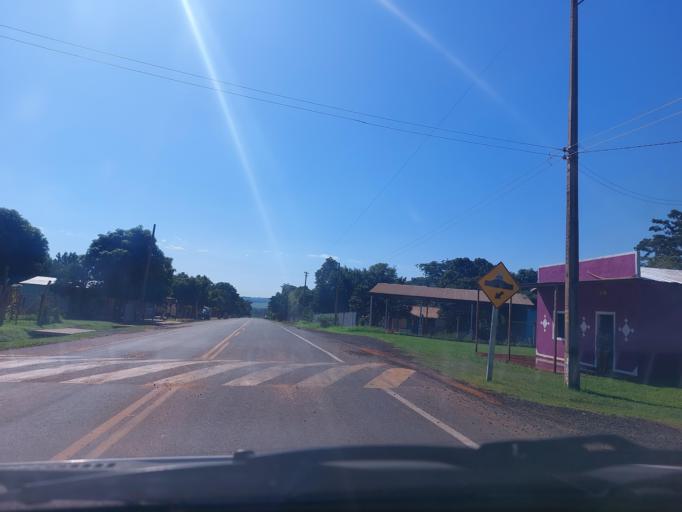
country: PY
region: San Pedro
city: Guayaybi
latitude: -24.3151
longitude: -56.1604
